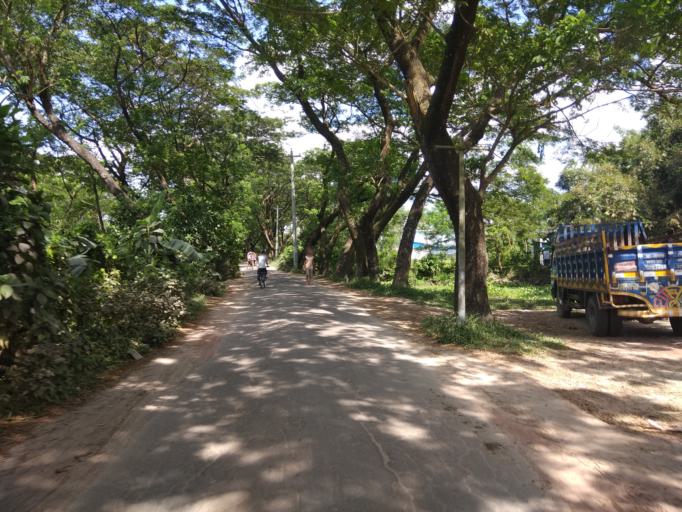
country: BD
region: Dhaka
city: Narayanganj
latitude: 23.5046
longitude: 90.4634
